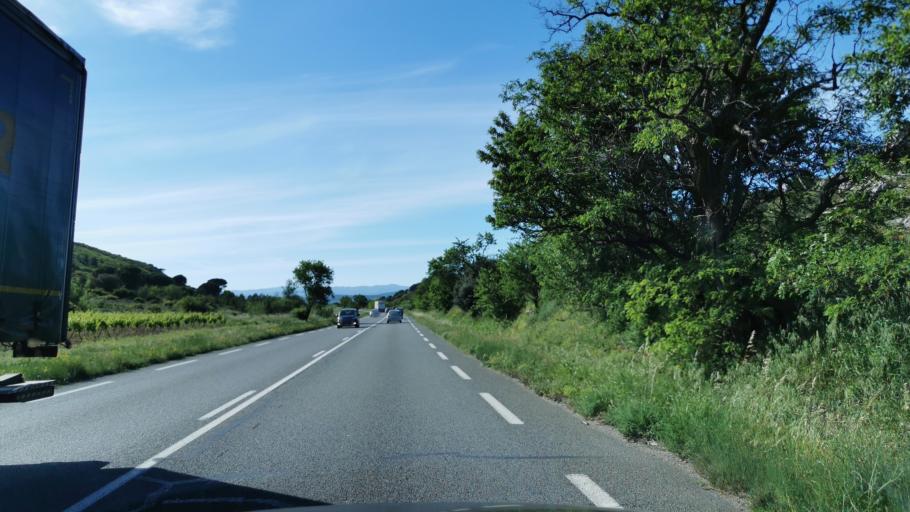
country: FR
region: Languedoc-Roussillon
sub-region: Departement de l'Aude
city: Nevian
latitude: 43.2036
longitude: 2.8895
